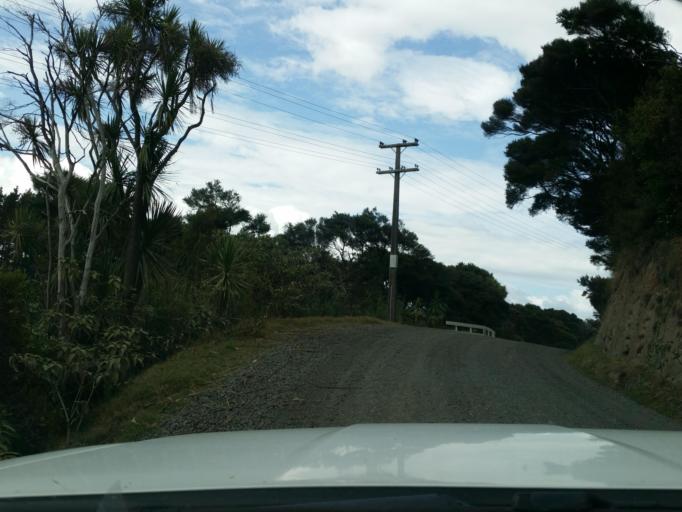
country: NZ
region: Auckland
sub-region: Auckland
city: Wellsford
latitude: -36.3162
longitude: 174.1344
